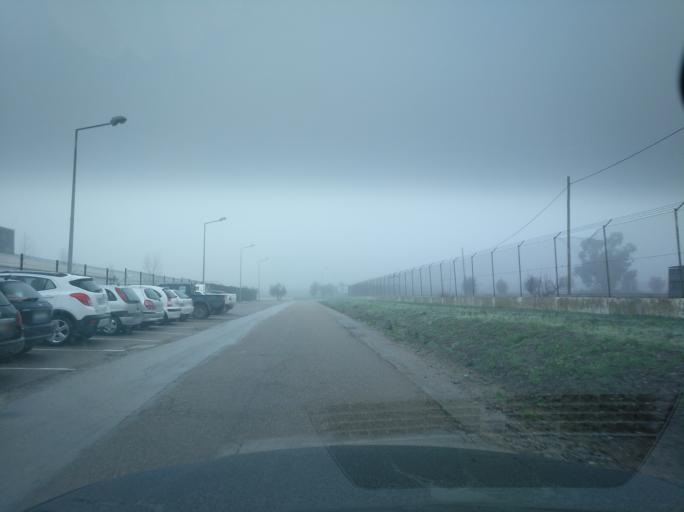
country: PT
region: Portalegre
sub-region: Campo Maior
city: Campo Maior
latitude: 39.0221
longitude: -7.0677
